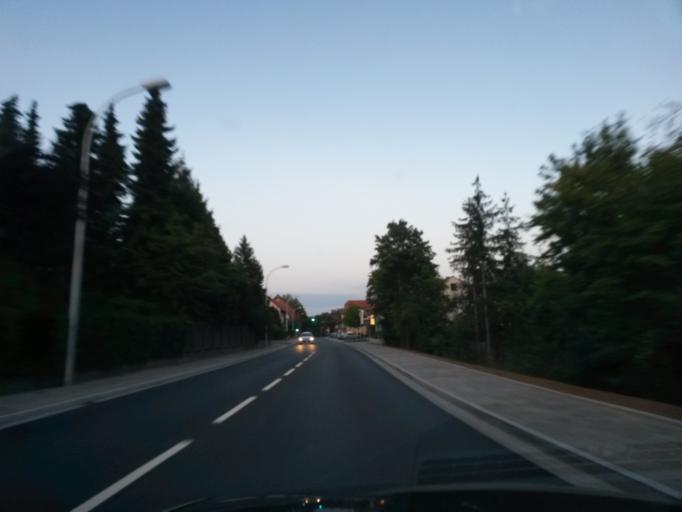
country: DE
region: Bavaria
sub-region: Regierungsbezirk Unterfranken
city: Uettingen
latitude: 49.7952
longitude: 9.7269
